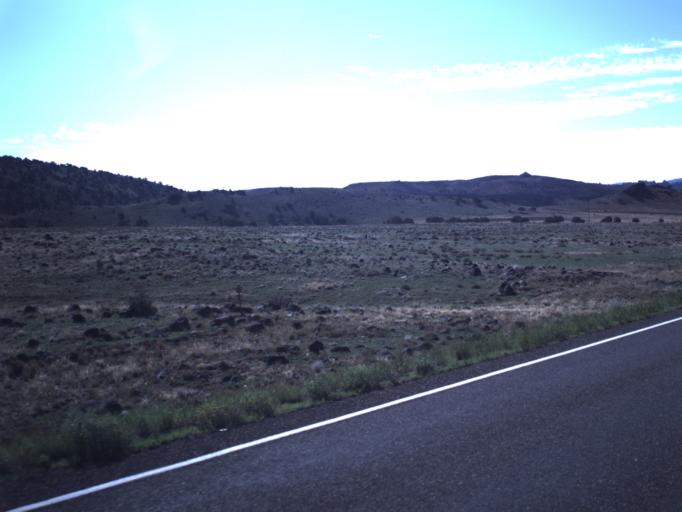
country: US
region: Utah
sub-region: Wayne County
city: Loa
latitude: 38.3232
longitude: -111.5299
